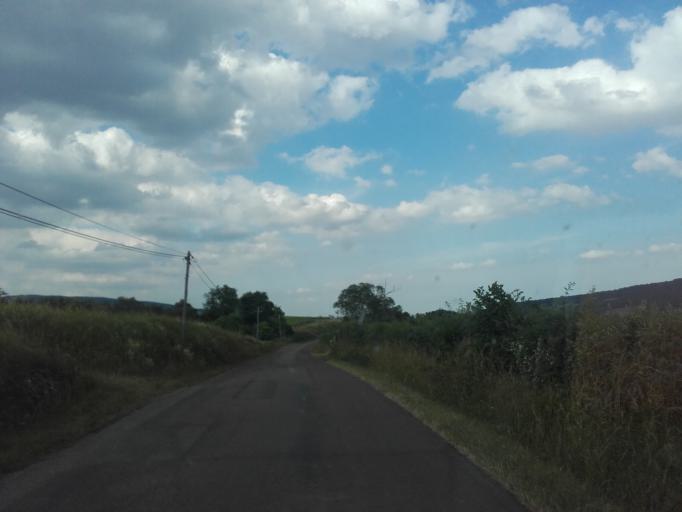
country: FR
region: Bourgogne
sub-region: Departement de Saone-et-Loire
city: Saint-Leger-sur-Dheune
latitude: 46.8884
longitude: 4.6523
